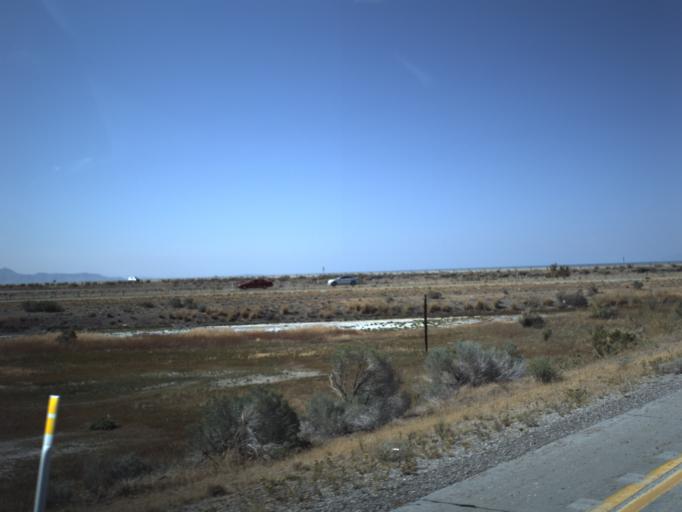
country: US
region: Utah
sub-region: Salt Lake County
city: Magna
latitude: 40.7468
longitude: -112.1793
